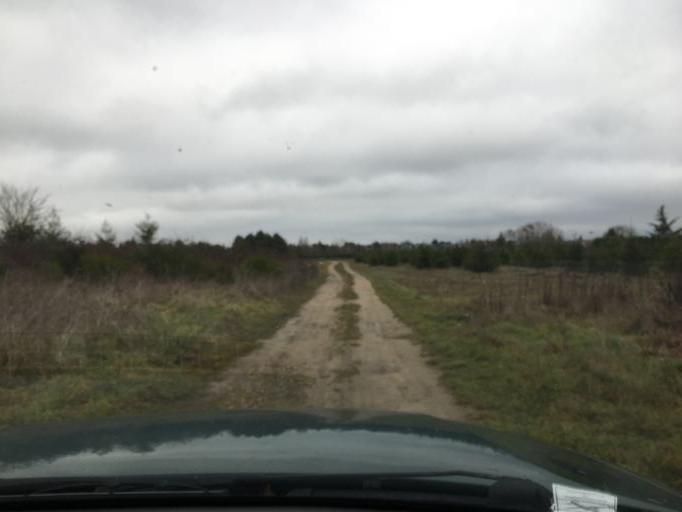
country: FR
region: Centre
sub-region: Departement du Loiret
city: Olivet
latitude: 47.8497
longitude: 1.8786
